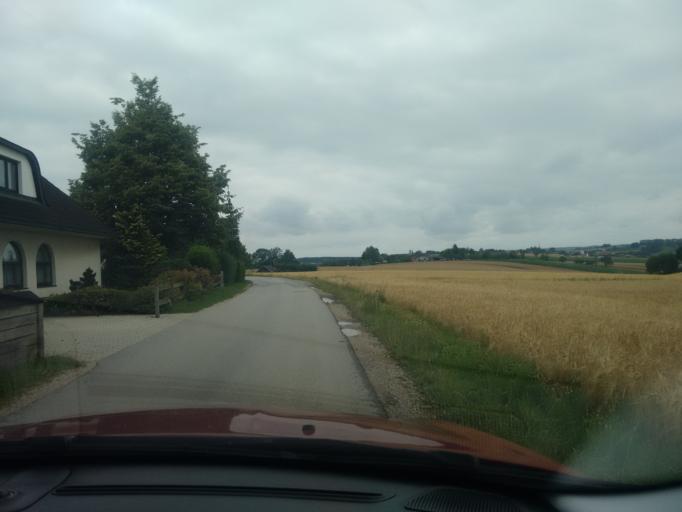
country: AT
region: Upper Austria
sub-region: Politischer Bezirk Steyr-Land
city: Bad Hall
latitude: 48.0402
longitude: 14.2281
